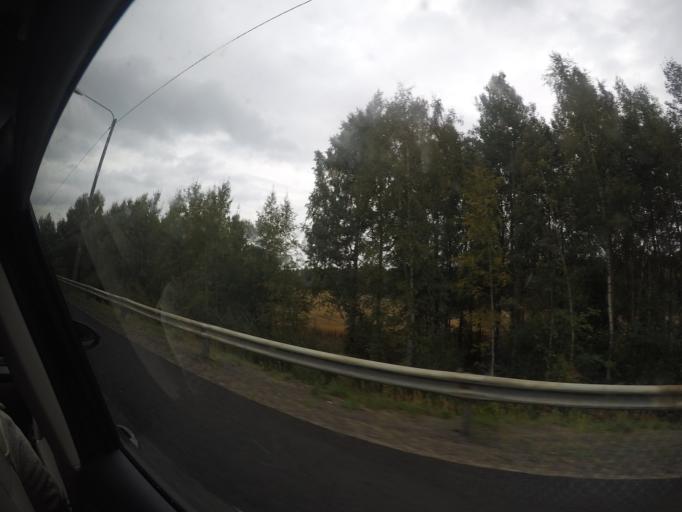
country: FI
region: Pirkanmaa
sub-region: Tampere
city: Kangasala
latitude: 61.4397
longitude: 24.1221
